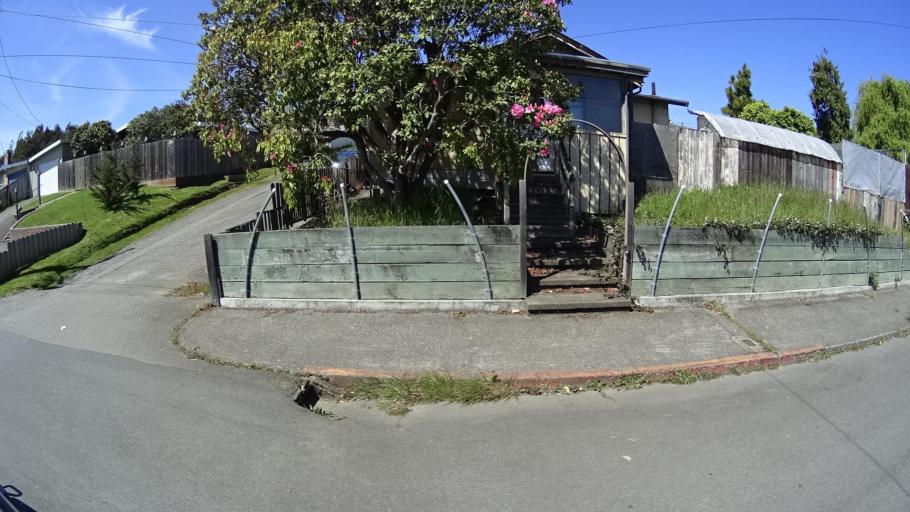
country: US
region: California
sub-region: Humboldt County
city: Eureka
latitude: 40.7929
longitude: -124.1482
